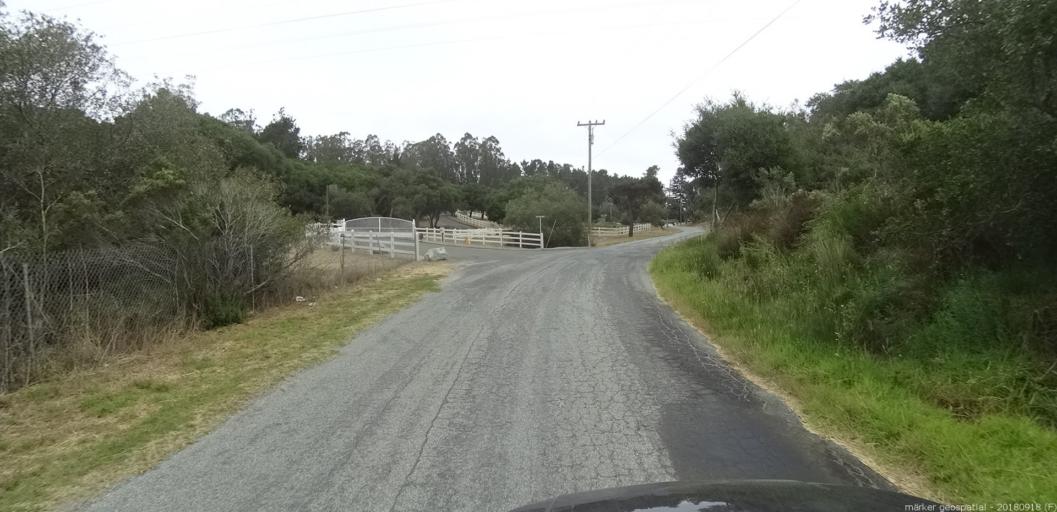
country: US
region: California
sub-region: Monterey County
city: Prunedale
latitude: 36.7810
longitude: -121.6495
